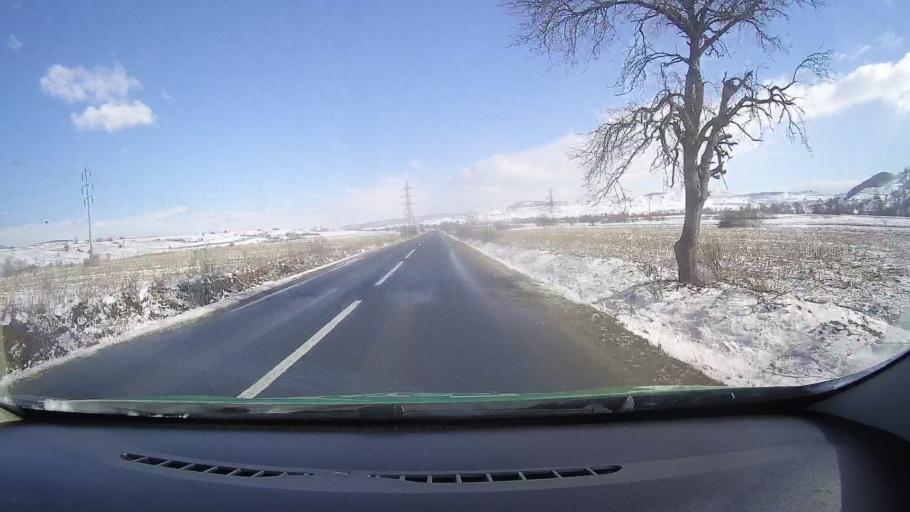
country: RO
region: Sibiu
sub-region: Comuna Rosia
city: Rosia
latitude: 45.7929
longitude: 24.3250
